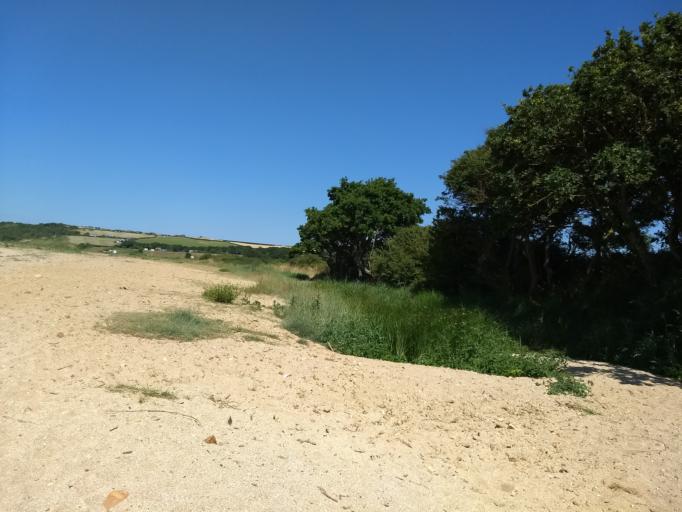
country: GB
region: England
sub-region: Isle of Wight
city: Gurnard
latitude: 50.7389
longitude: -1.3536
